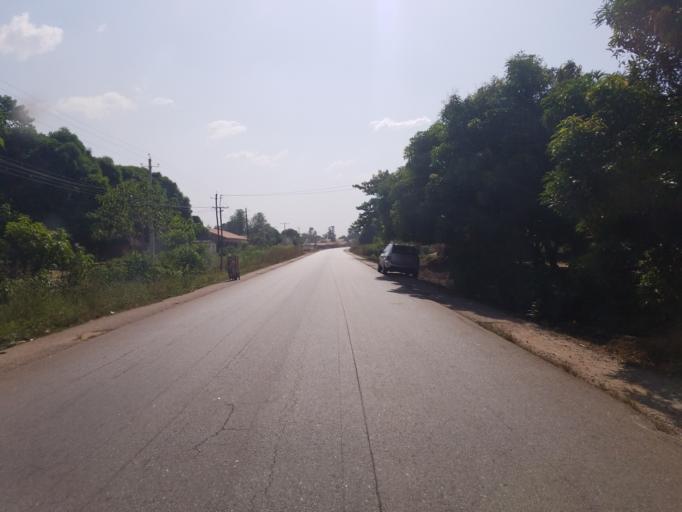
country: GN
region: Boke
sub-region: Fria
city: Fria
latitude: 10.0773
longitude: -13.7011
